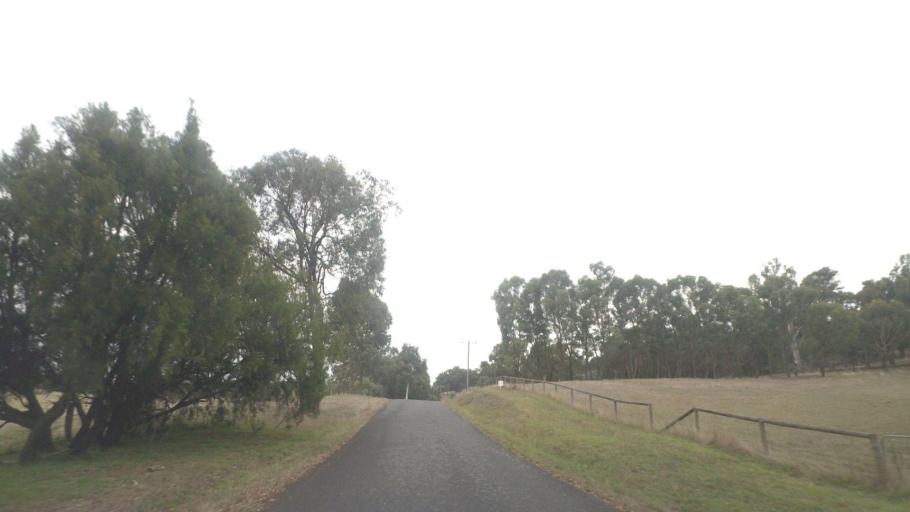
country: AU
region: Victoria
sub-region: Nillumbik
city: North Warrandyte
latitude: -37.7377
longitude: 145.1856
